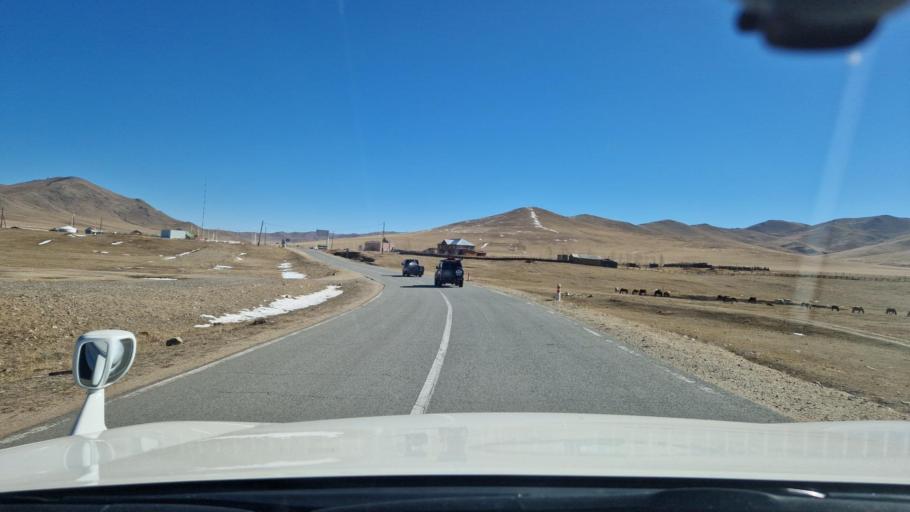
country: MN
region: Central Aimak
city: Bayandelger
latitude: 47.6928
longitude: 108.4725
